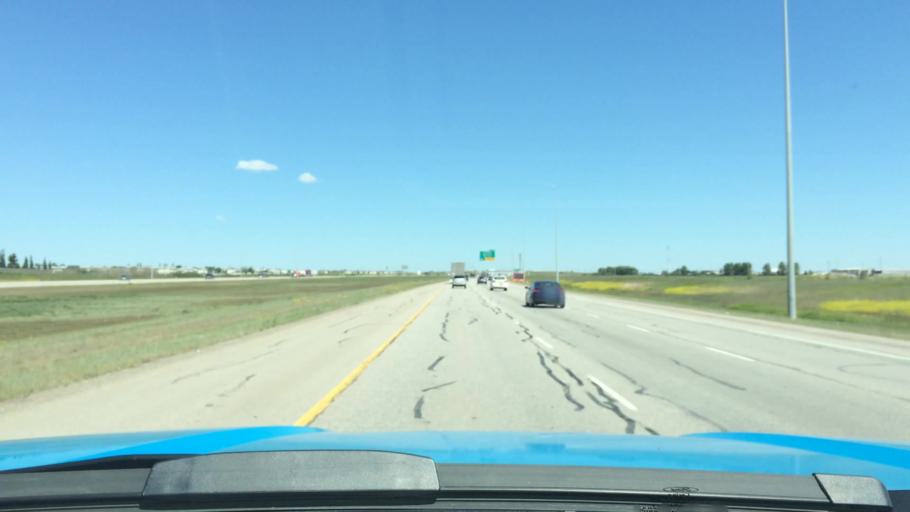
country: CA
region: Alberta
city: Chestermere
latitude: 51.0770
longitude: -113.9203
